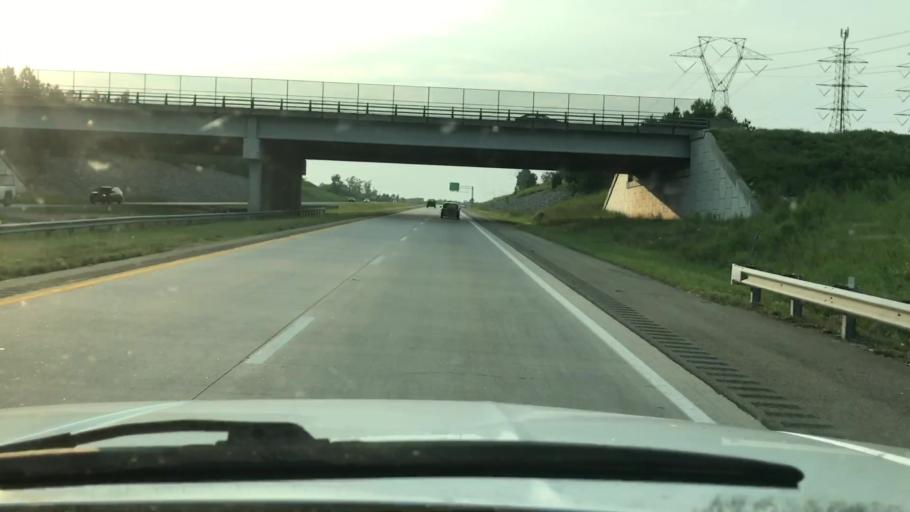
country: US
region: Virginia
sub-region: Chesterfield County
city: Brandermill
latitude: 37.4886
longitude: -77.6727
